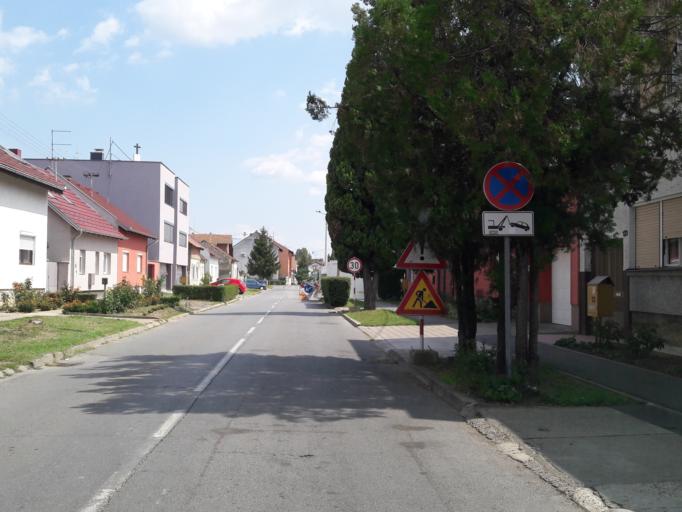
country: HR
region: Osjecko-Baranjska
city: Visnjevac
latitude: 45.5612
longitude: 18.6459
